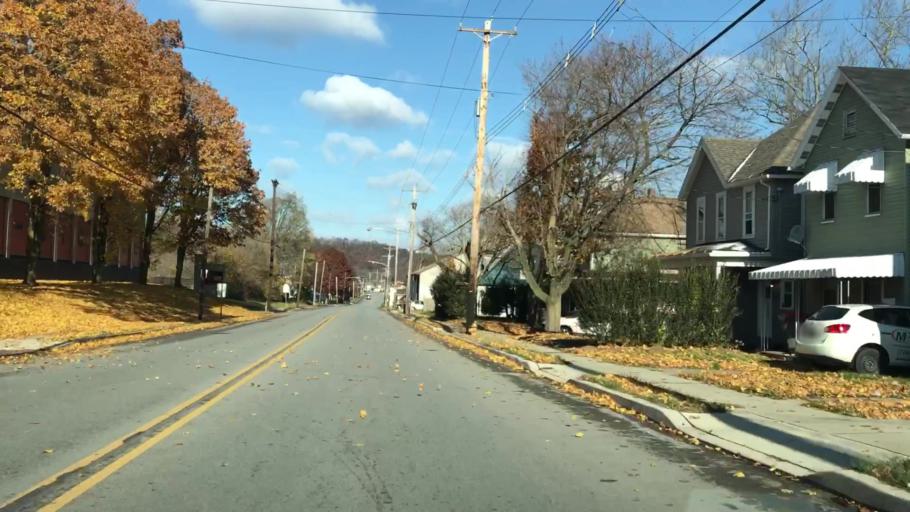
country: US
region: Pennsylvania
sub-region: Beaver County
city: West Mayfield
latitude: 40.7811
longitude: -80.3265
